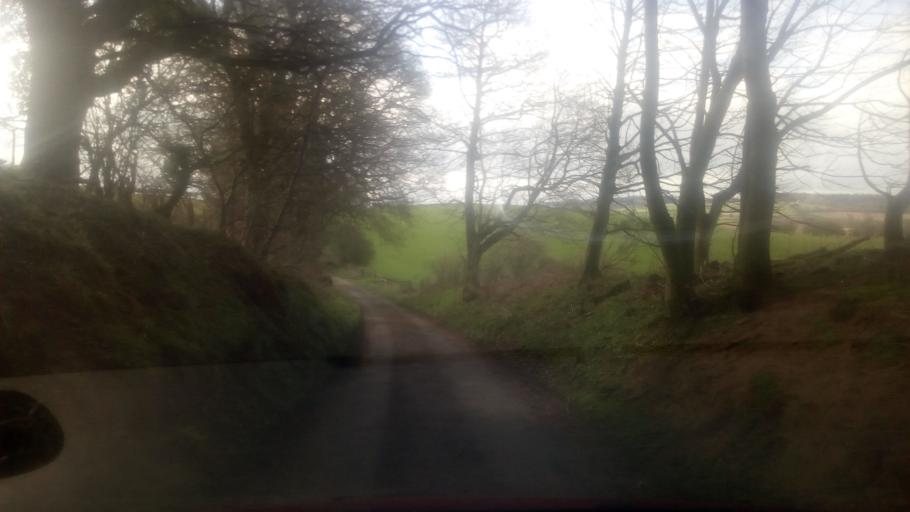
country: GB
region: Scotland
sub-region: The Scottish Borders
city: Jedburgh
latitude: 55.4963
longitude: -2.5351
